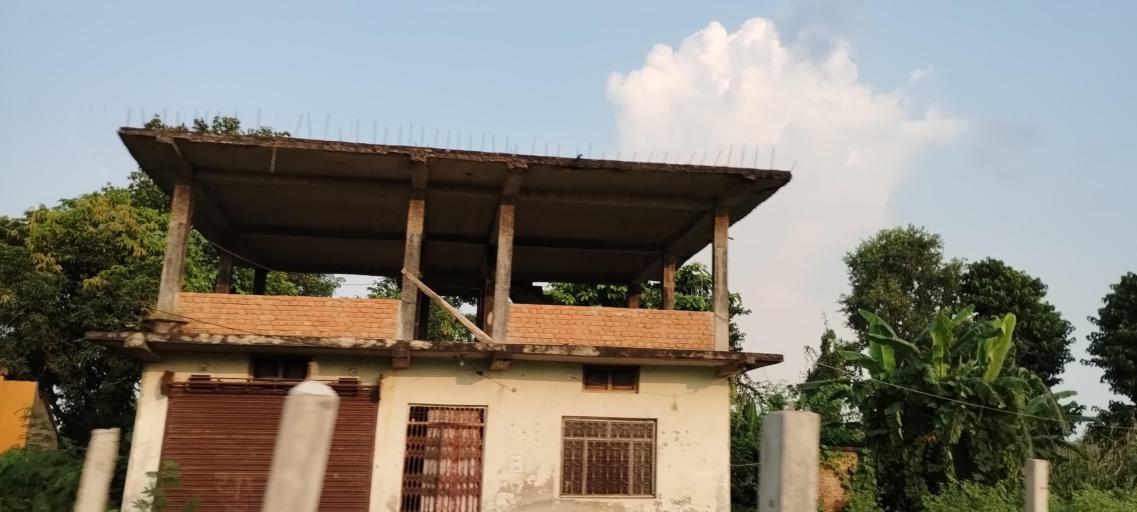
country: NP
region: Far Western
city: Tikapur
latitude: 28.4722
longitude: 81.2783
